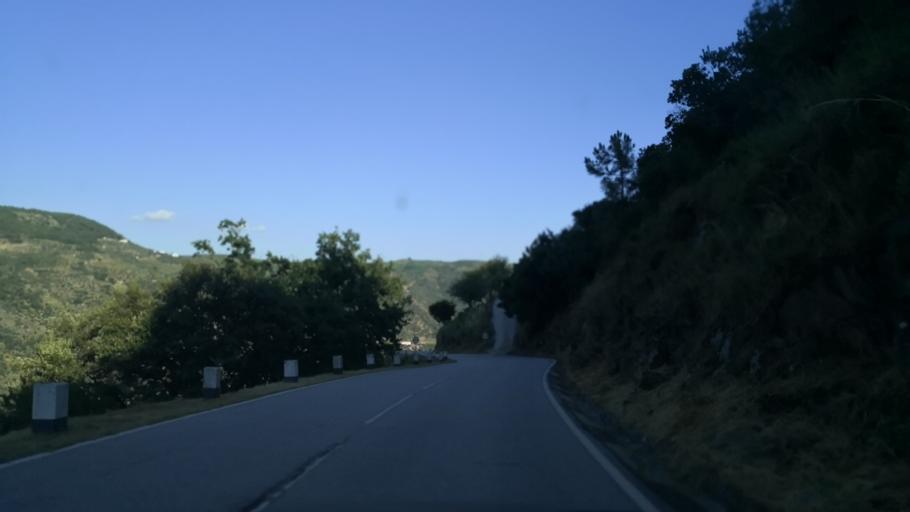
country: PT
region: Viseu
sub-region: Sao Joao da Pesqueira
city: Sao Joao da Pesqueira
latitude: 41.2409
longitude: -7.4326
